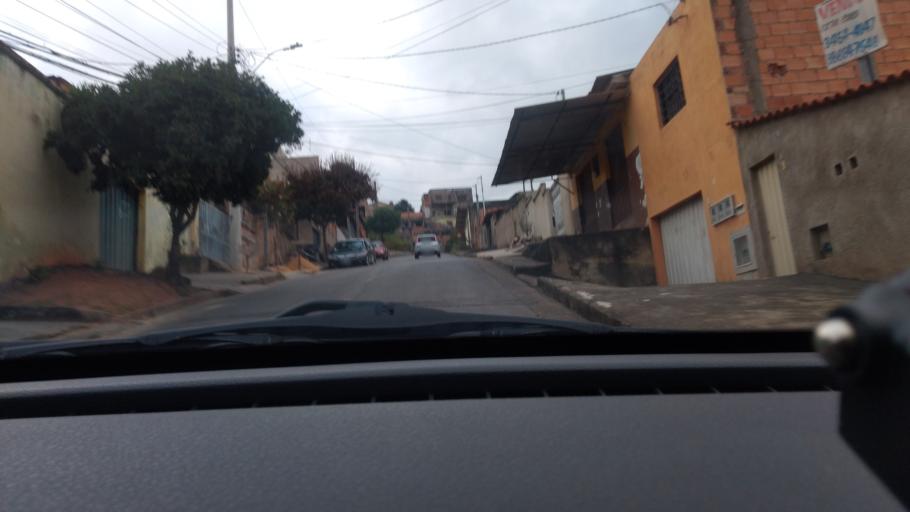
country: BR
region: Minas Gerais
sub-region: Santa Luzia
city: Santa Luzia
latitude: -19.8159
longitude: -43.9373
